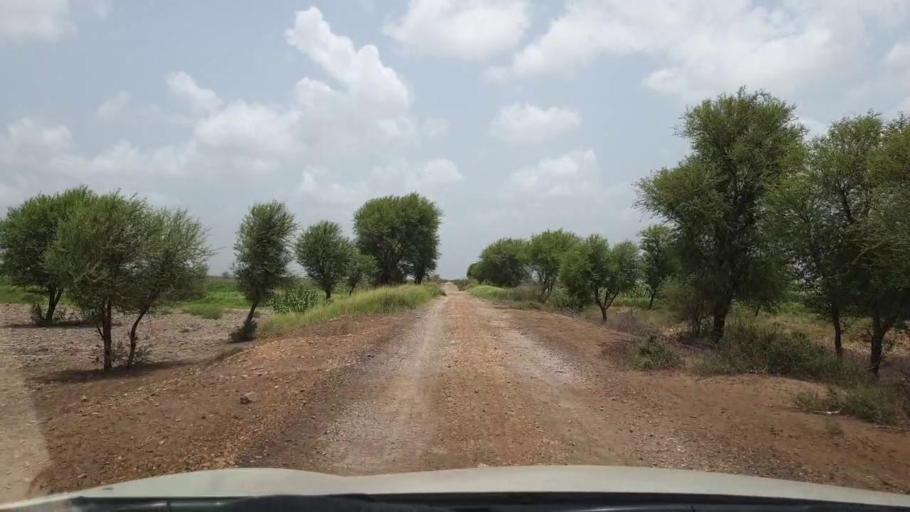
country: PK
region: Sindh
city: Chambar
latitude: 25.2182
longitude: 68.7595
